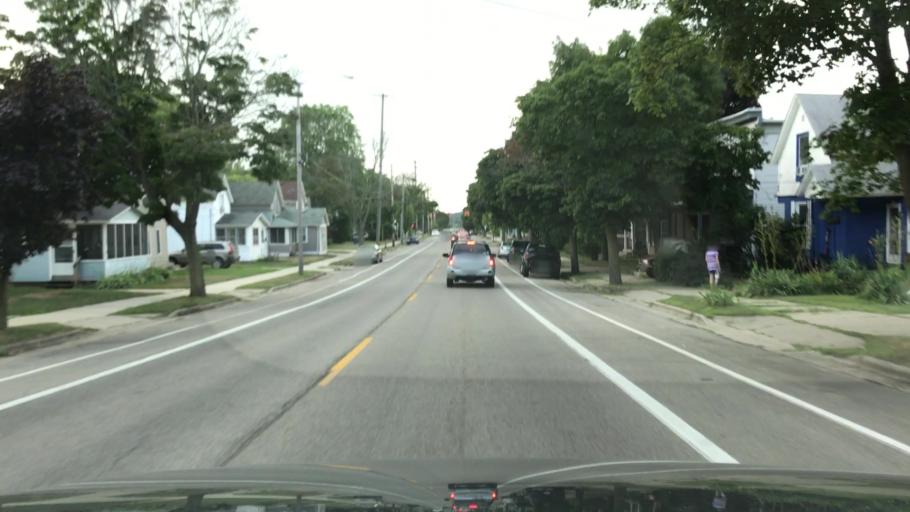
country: US
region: Michigan
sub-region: Kent County
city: Grand Rapids
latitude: 42.9955
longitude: -85.6626
